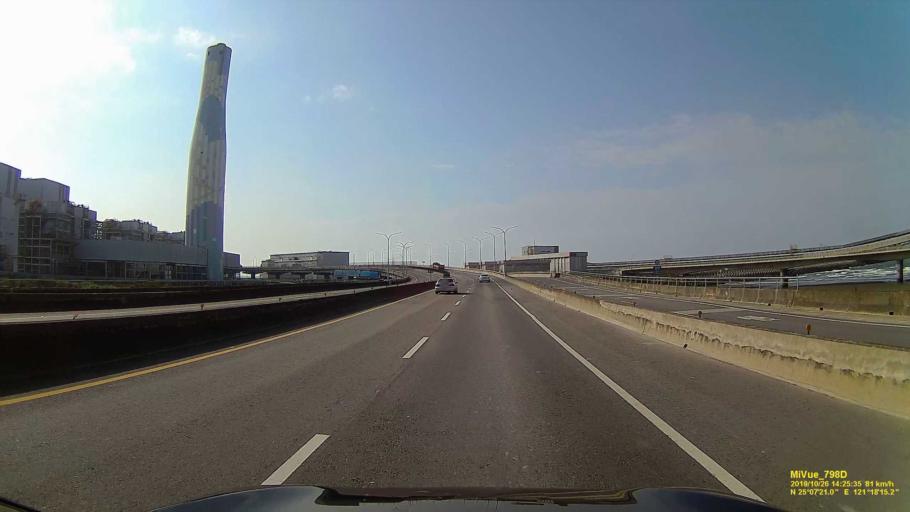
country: TW
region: Taiwan
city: Taoyuan City
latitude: 25.1226
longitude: 121.3038
